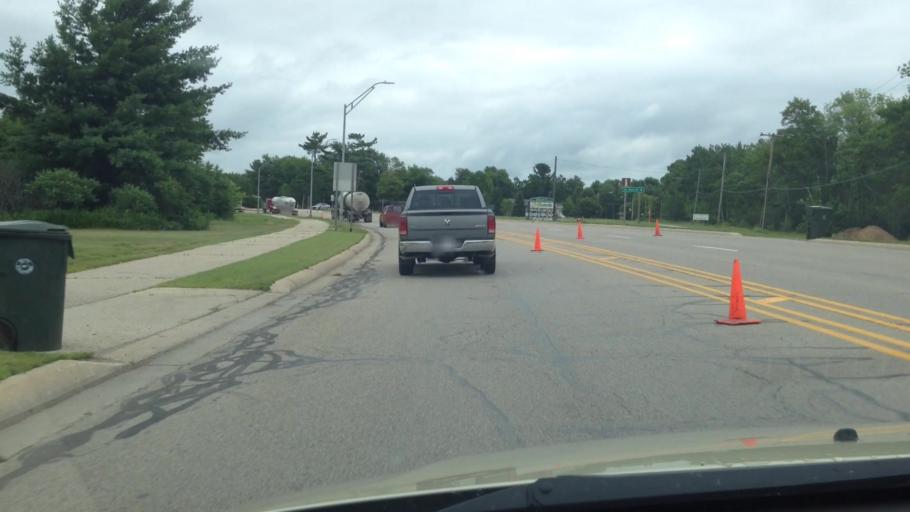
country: US
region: Michigan
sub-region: Delta County
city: Escanaba
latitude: 45.7147
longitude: -87.0835
